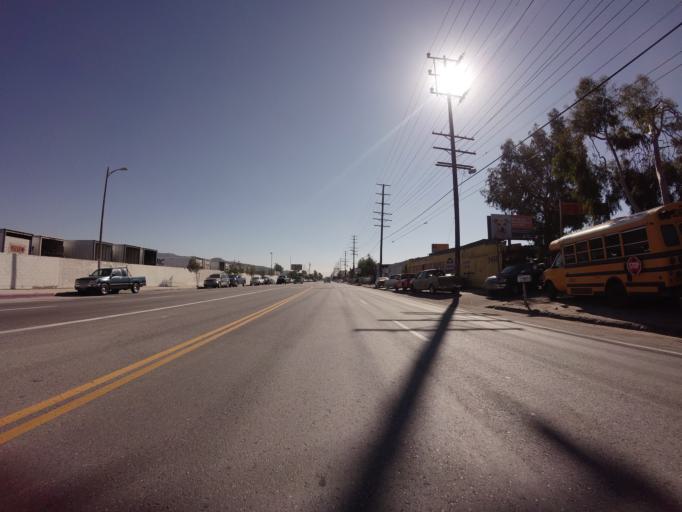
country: US
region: California
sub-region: Los Angeles County
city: North Hollywood
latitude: 34.2403
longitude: -118.3775
